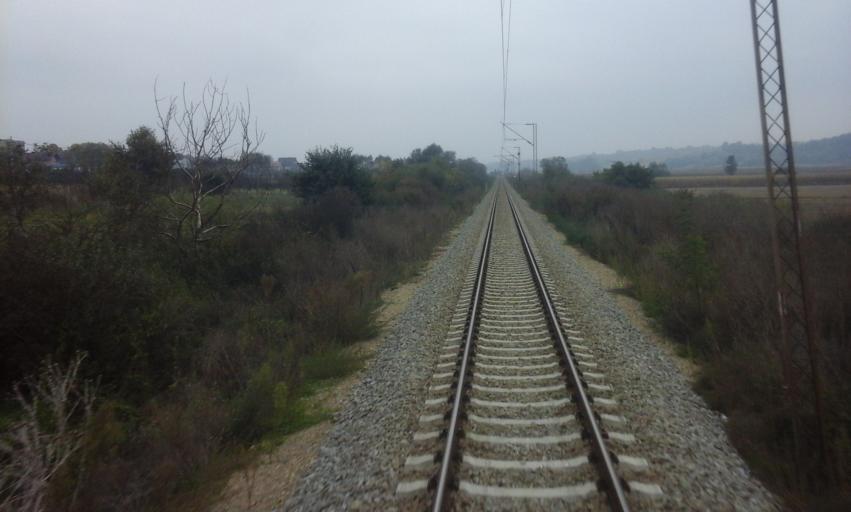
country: RS
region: Central Serbia
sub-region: Belgrade
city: Mladenovac
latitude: 44.4682
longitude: 20.6638
